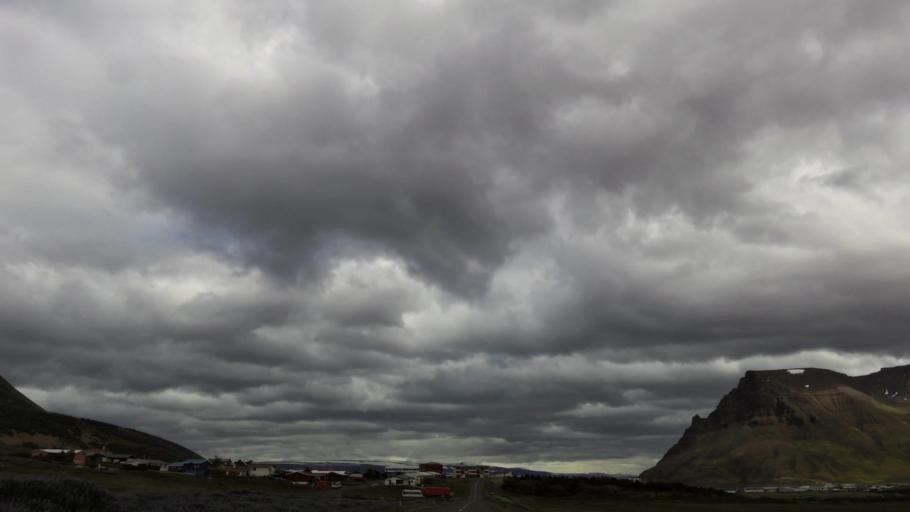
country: IS
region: Westfjords
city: Isafjoerdur
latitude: 66.1587
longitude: -23.2721
